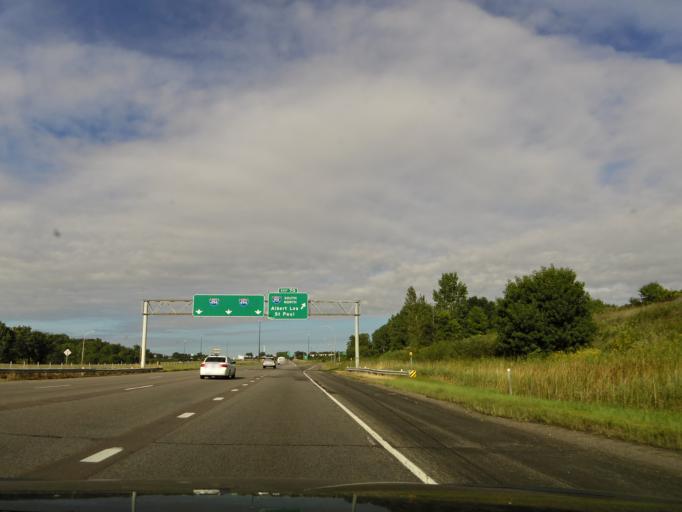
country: US
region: Minnesota
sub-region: Dakota County
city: Mendota Heights
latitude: 44.8630
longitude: -93.1351
